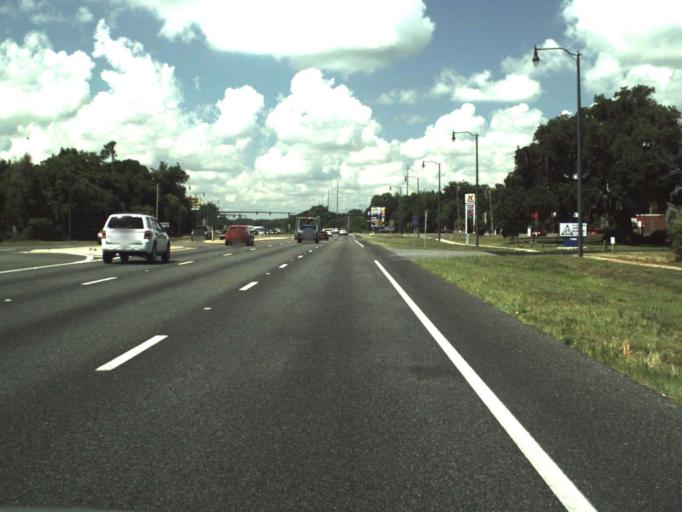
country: US
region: Florida
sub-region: Lake County
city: Silver Lake
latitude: 28.8268
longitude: -81.8290
